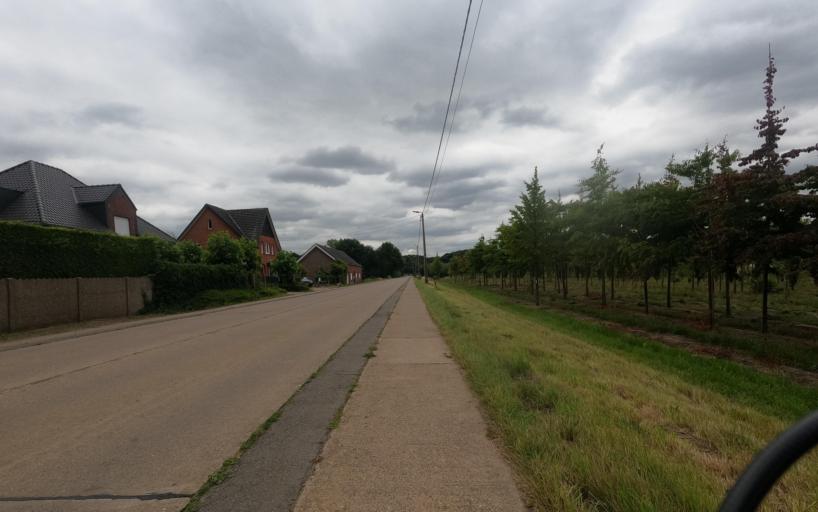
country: BE
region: Flanders
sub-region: Provincie Vlaams-Brabant
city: Begijnendijk
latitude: 50.9762
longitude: 4.7813
